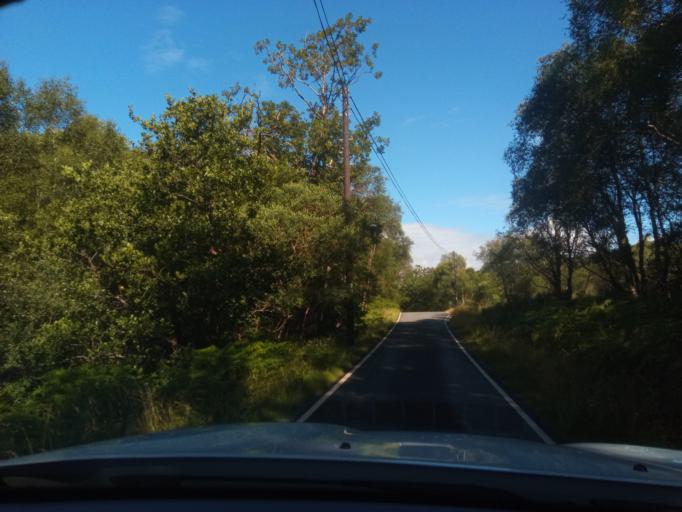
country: GB
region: Scotland
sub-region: Argyll and Bute
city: Isle Of Mull
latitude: 56.6868
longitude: -5.6586
